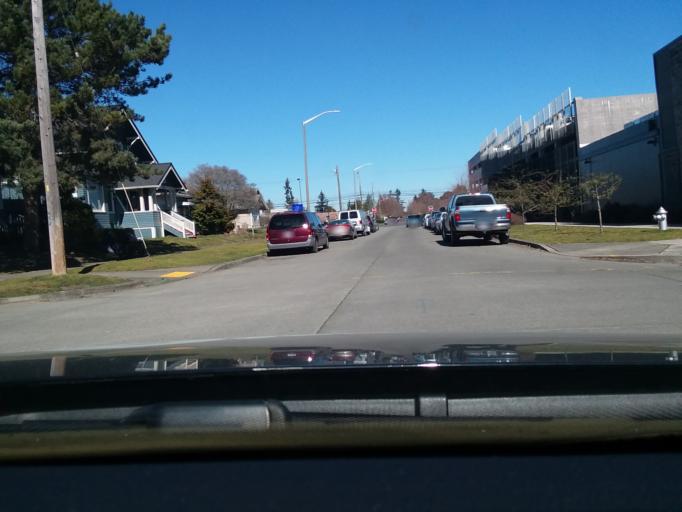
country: US
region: Washington
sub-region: Pierce County
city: Tacoma
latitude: 47.2497
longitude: -122.4526
